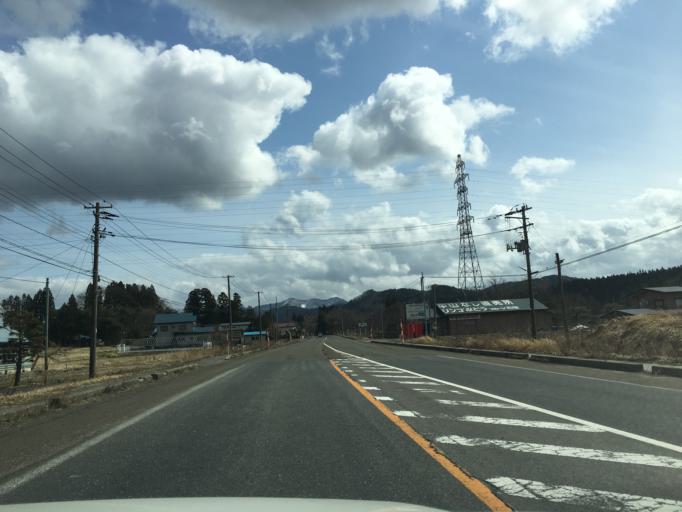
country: JP
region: Akita
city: Odate
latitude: 40.2274
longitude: 140.5992
